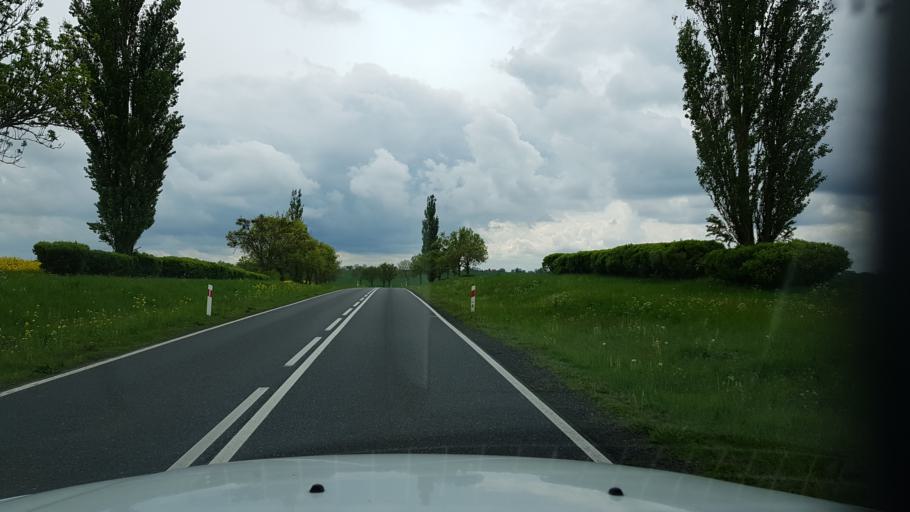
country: PL
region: West Pomeranian Voivodeship
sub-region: Powiat gryfinski
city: Moryn
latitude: 52.8820
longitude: 14.4729
